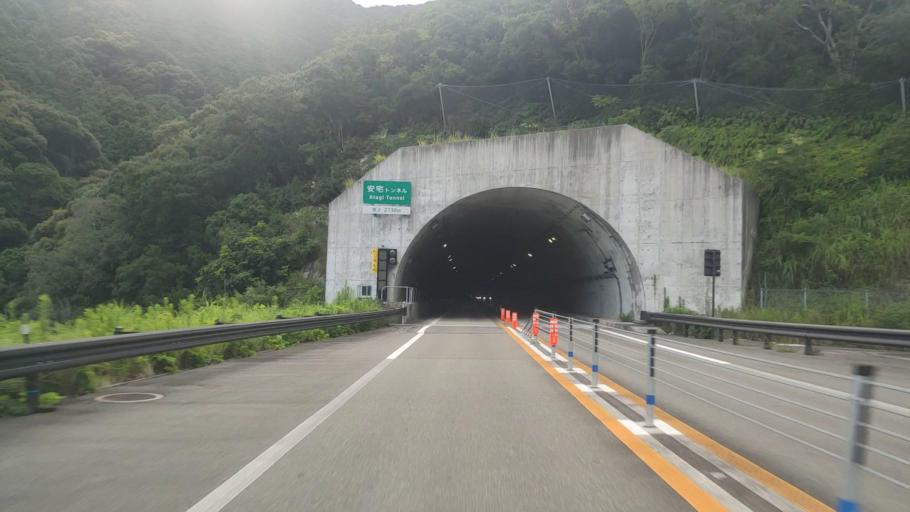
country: JP
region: Wakayama
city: Tanabe
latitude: 33.5665
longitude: 135.4929
